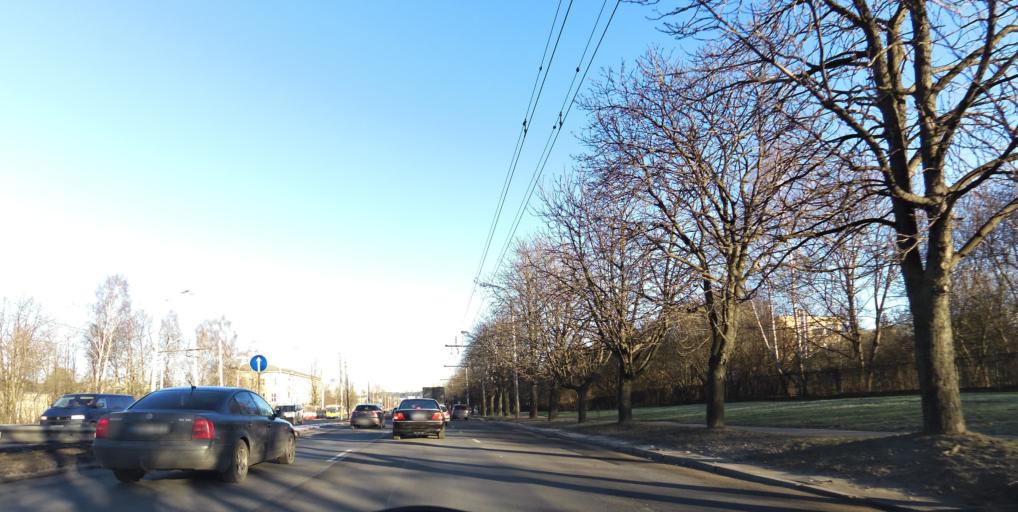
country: LT
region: Vilnius County
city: Lazdynai
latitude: 54.6454
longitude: 25.2086
